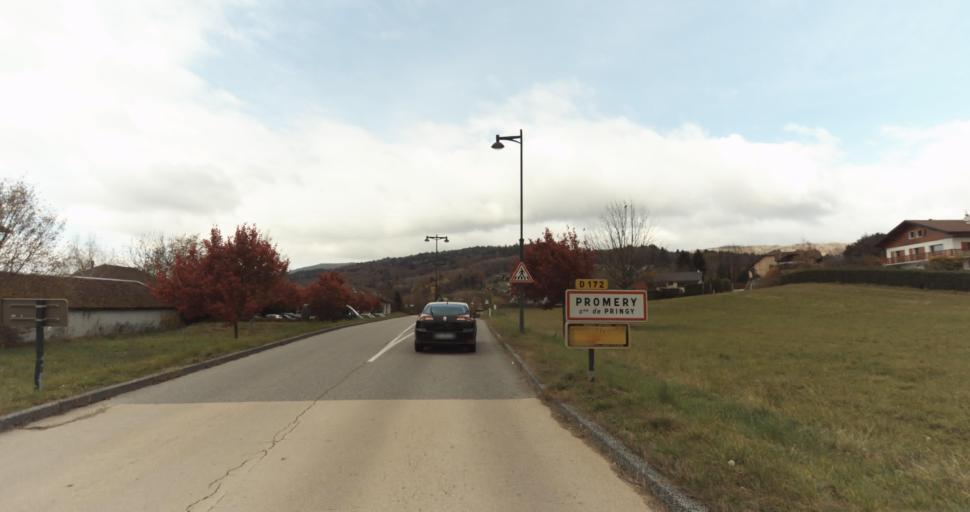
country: FR
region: Rhone-Alpes
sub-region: Departement de la Haute-Savoie
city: Pringy
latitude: 45.9550
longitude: 6.1139
